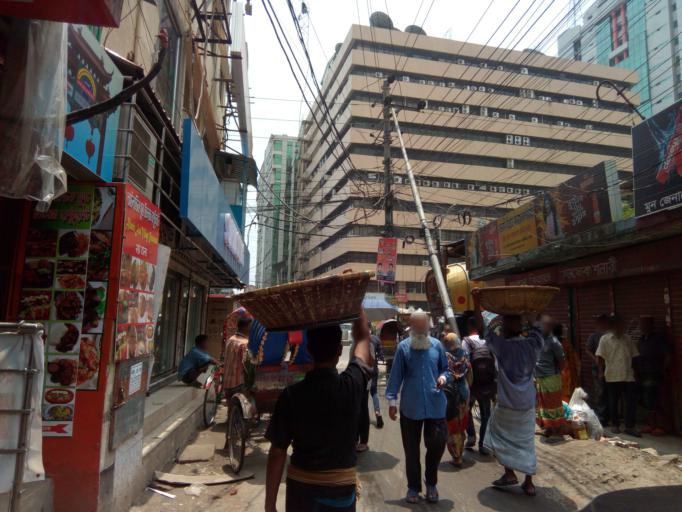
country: BD
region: Dhaka
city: Azimpur
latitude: 23.7516
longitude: 90.3922
